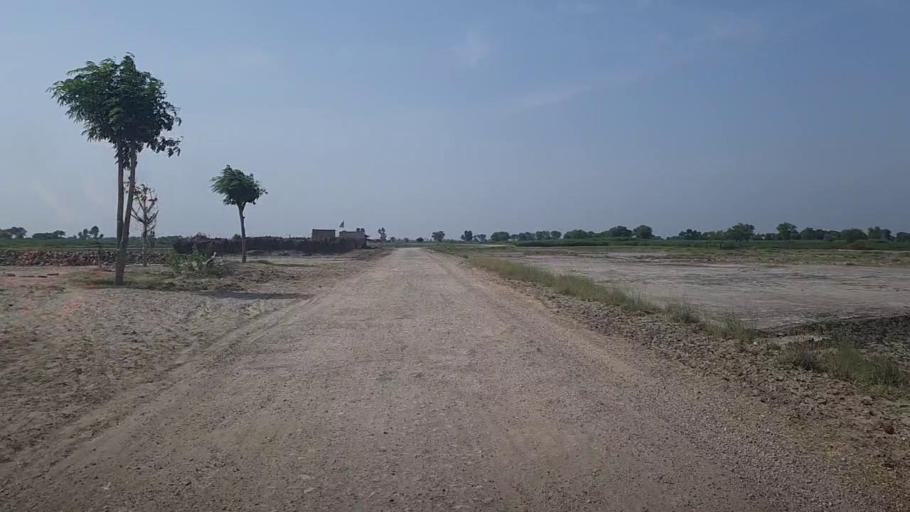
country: PK
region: Sindh
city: Ubauro
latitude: 28.1402
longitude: 69.8134
